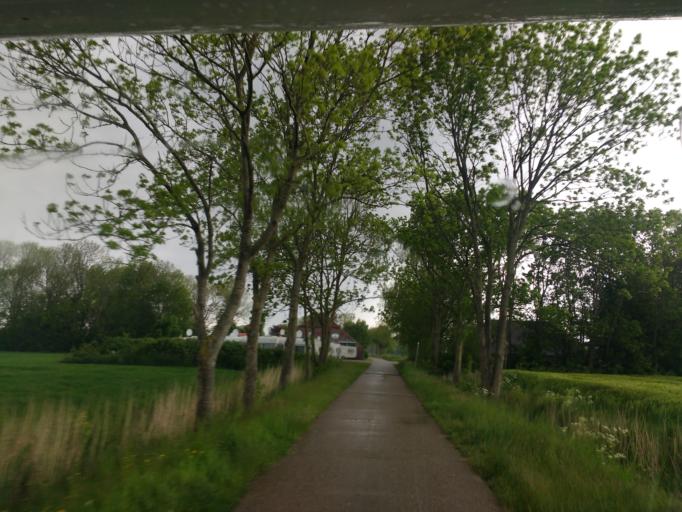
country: DE
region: Lower Saxony
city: Schillig
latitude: 53.6996
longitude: 7.9999
